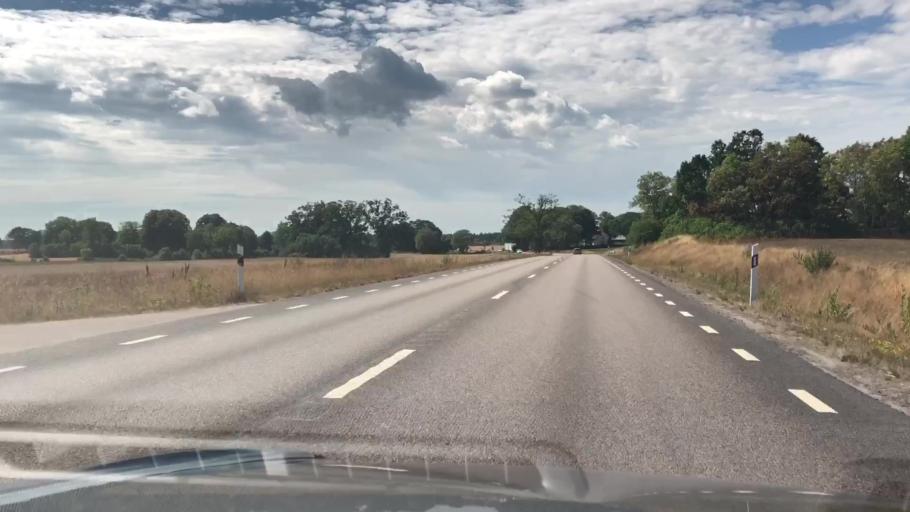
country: SE
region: Kalmar
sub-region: Torsas Kommun
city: Torsas
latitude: 56.4256
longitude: 16.0735
